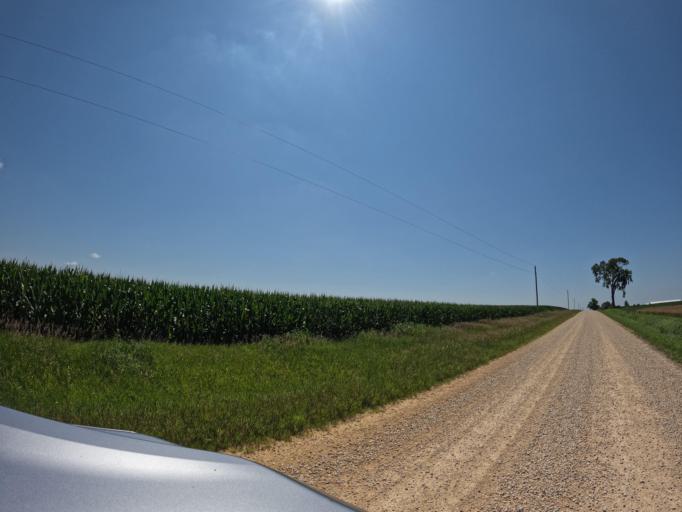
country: US
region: Iowa
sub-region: Clinton County
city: Camanche
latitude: 41.8004
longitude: -90.3938
